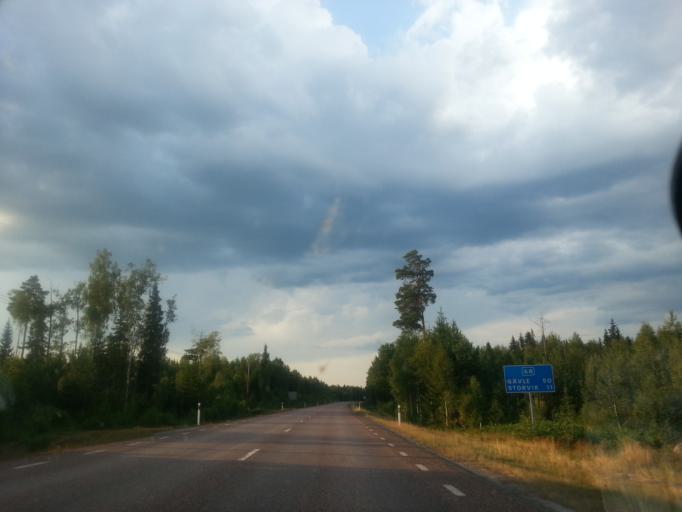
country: SE
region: Gaevleborg
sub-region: Hofors Kommun
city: Hofors
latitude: 60.5025
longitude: 16.4325
